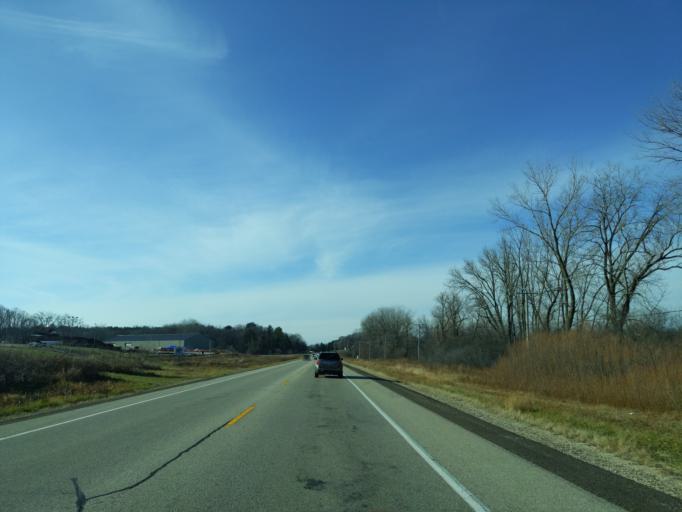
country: US
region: Wisconsin
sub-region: Rock County
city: Milton
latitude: 42.8263
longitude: -88.9954
